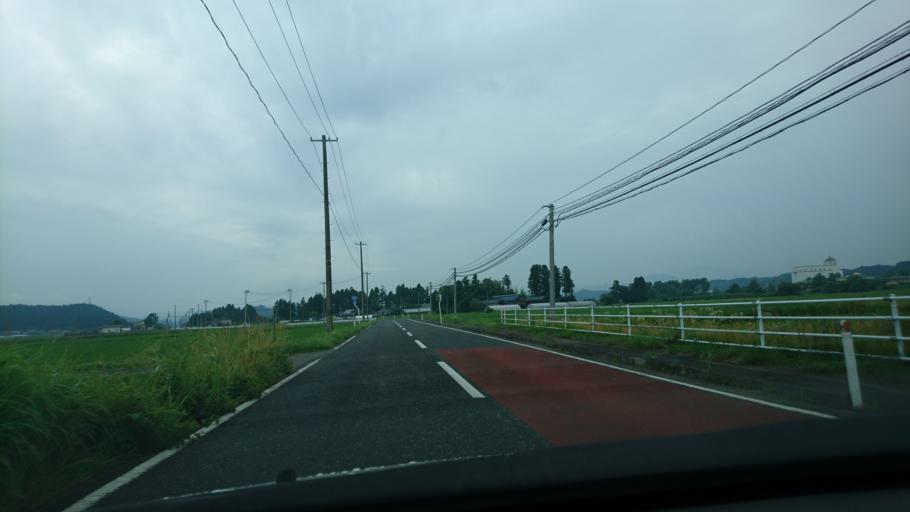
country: JP
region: Miyagi
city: Furukawa
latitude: 38.7392
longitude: 140.9432
